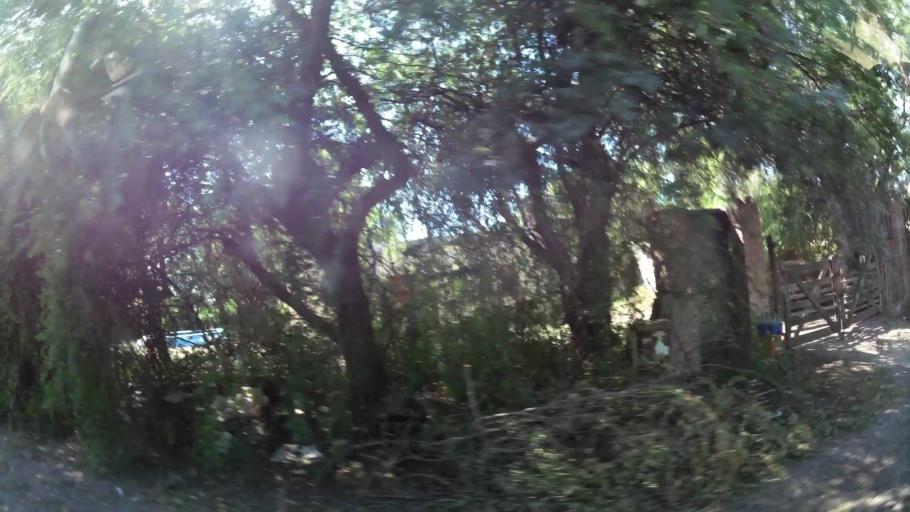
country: AR
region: Cordoba
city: Villa Allende
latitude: -31.2951
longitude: -64.2824
